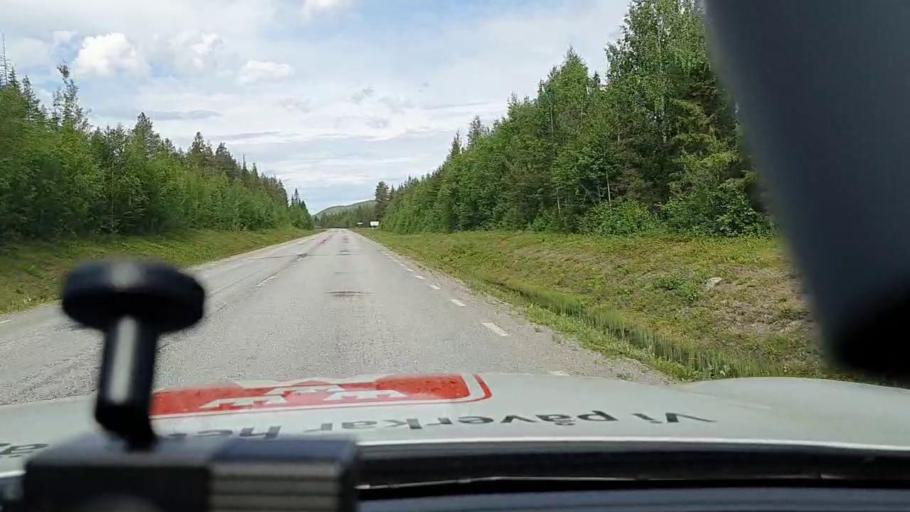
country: SE
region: Norrbotten
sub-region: Jokkmokks Kommun
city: Jokkmokk
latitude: 66.5510
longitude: 20.1202
